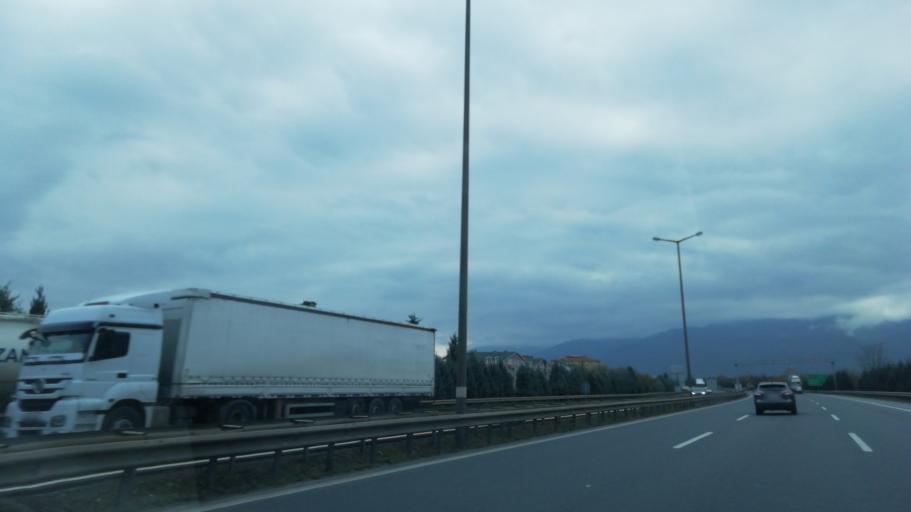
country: TR
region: Kocaeli
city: Kosekoy
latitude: 40.7425
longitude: 30.0435
